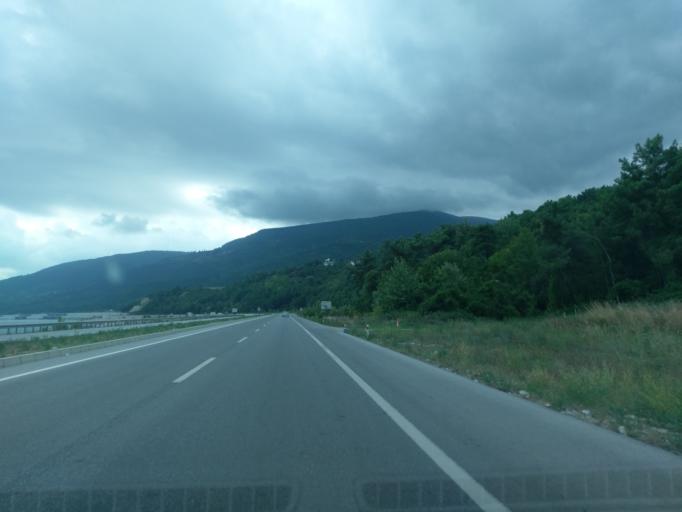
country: TR
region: Sinop
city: Gerze
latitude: 41.7784
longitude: 35.2024
